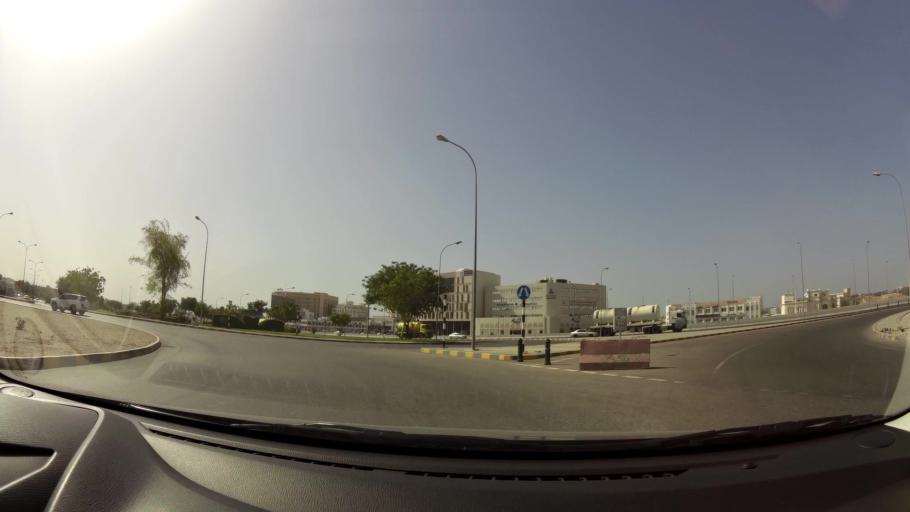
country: OM
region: Muhafazat Masqat
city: Muscat
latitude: 23.6090
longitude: 58.4967
